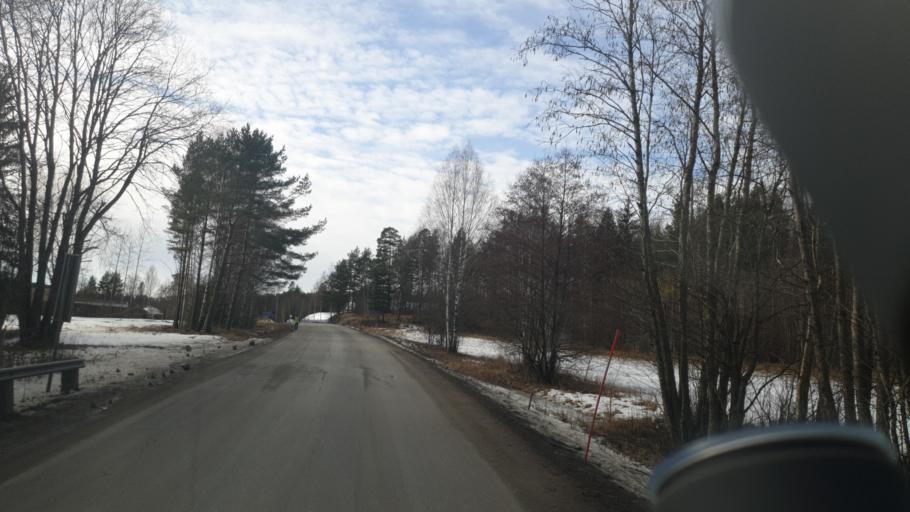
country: SE
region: Vaermland
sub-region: Arvika Kommun
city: Arvika
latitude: 59.6654
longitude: 12.6365
